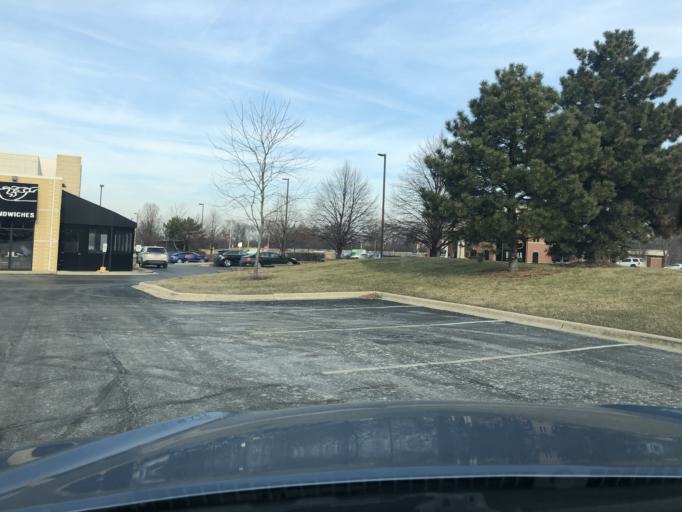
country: US
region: Illinois
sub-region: DuPage County
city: Itasca
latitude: 41.9866
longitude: -88.0039
